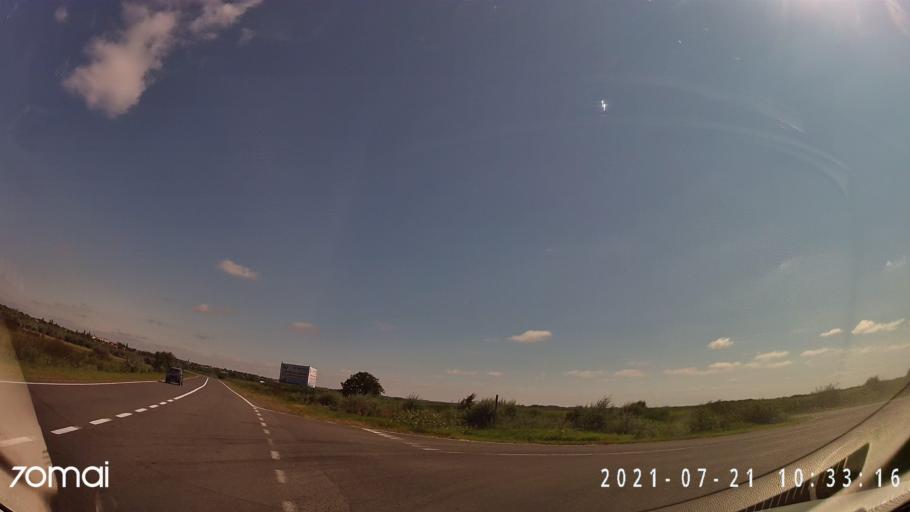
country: RO
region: Tulcea
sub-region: Oras Isaccea
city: Isaccea
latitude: 45.3026
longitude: 28.4364
